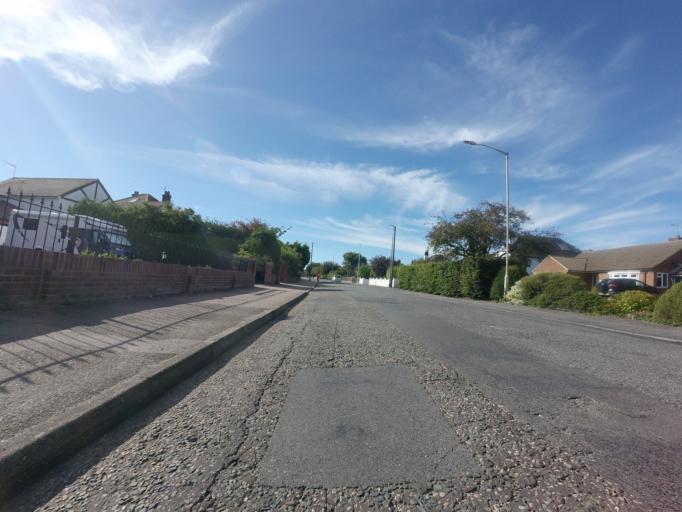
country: GB
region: England
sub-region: Kent
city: Herne Bay
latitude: 51.3687
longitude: 1.1497
